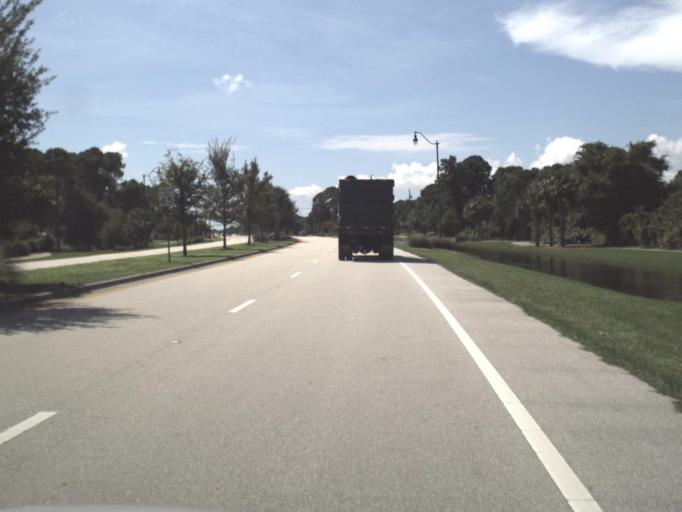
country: US
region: Florida
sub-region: Sarasota County
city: North Port
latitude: 27.0382
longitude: -82.1634
